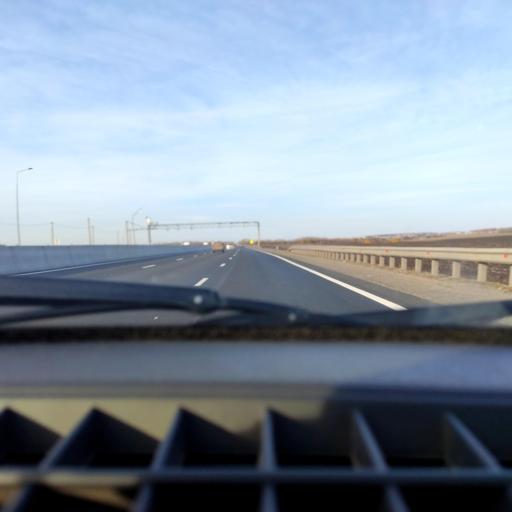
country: RU
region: Bashkortostan
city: Avdon
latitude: 54.6739
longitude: 55.7810
